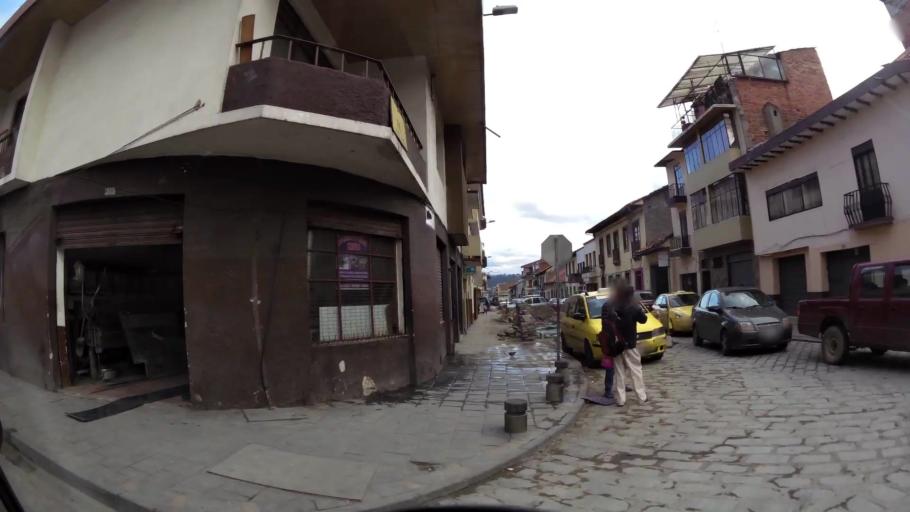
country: EC
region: Azuay
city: Cuenca
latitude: -2.8929
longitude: -78.9991
